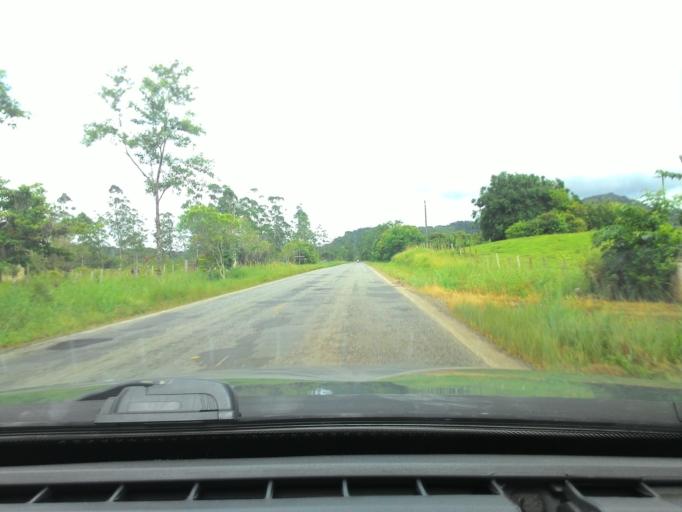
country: BR
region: Sao Paulo
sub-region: Pariquera-Acu
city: Pariquera Acu
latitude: -24.7328
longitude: -47.8254
